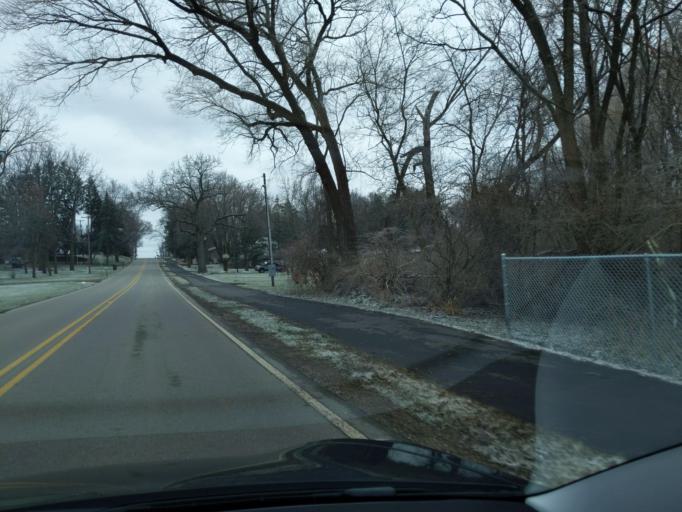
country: US
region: Michigan
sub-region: Jackson County
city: Spring Arbor
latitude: 42.2012
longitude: -84.5537
